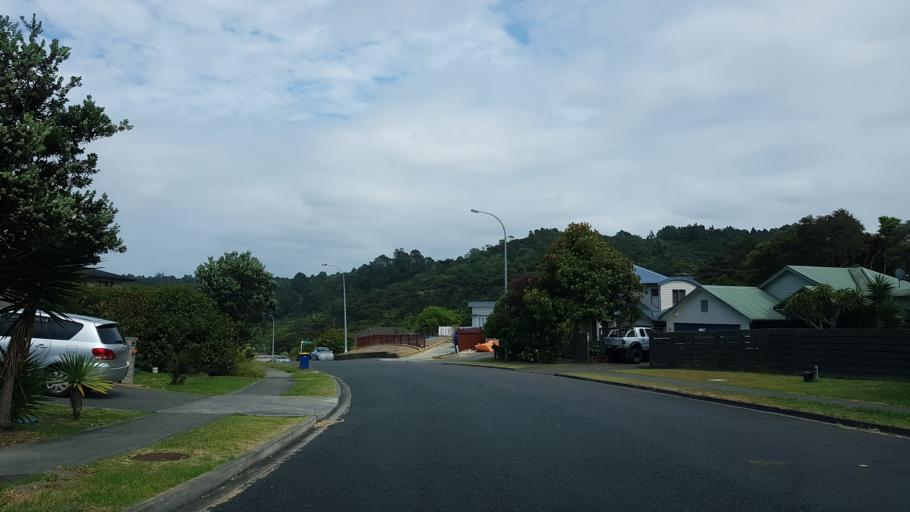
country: NZ
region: Auckland
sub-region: Auckland
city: North Shore
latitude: -36.7692
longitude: 174.7096
